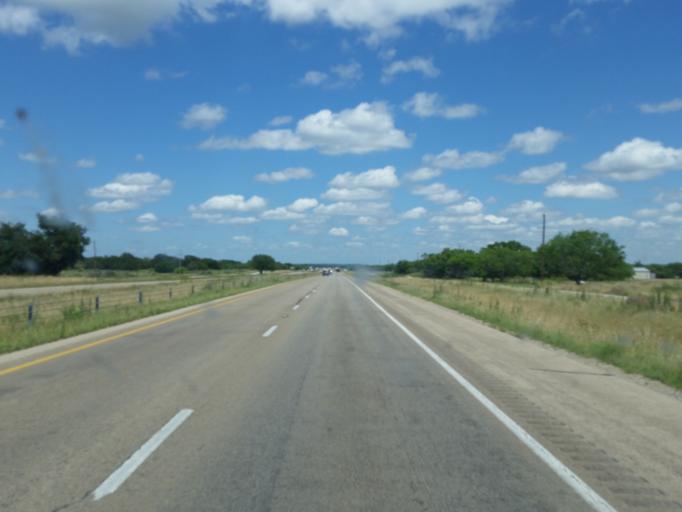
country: US
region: Texas
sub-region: Callahan County
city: Baird
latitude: 32.3892
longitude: -99.3264
